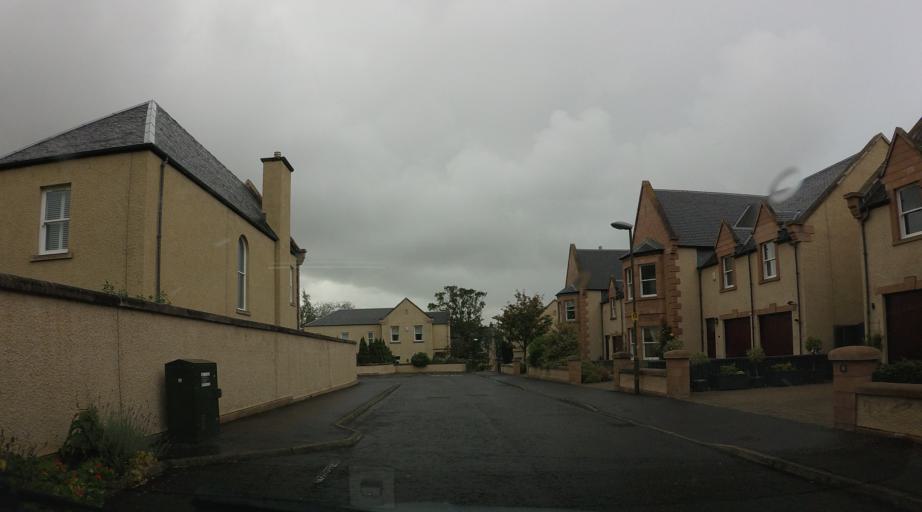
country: GB
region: Scotland
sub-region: East Lothian
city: Musselburgh
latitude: 55.9321
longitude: -3.0438
